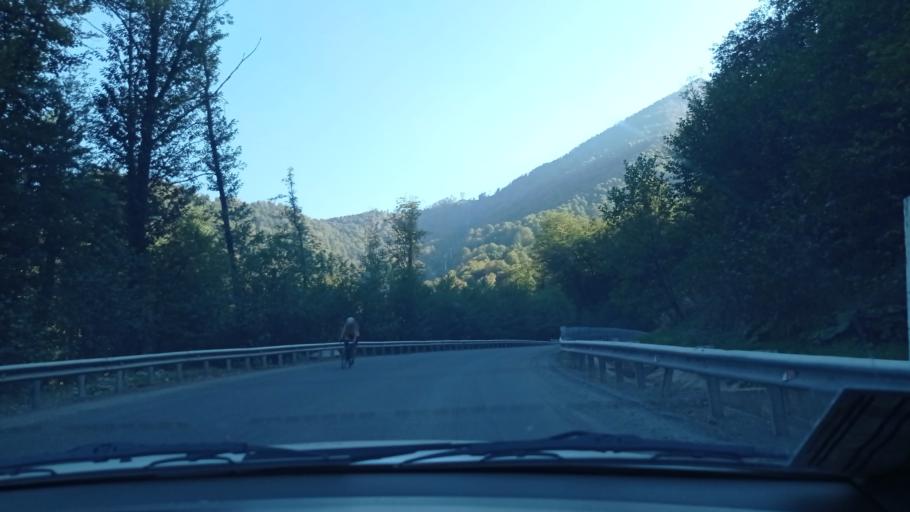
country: RU
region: Krasnodarskiy
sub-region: Sochi City
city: Krasnaya Polyana
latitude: 43.6609
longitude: 40.2999
